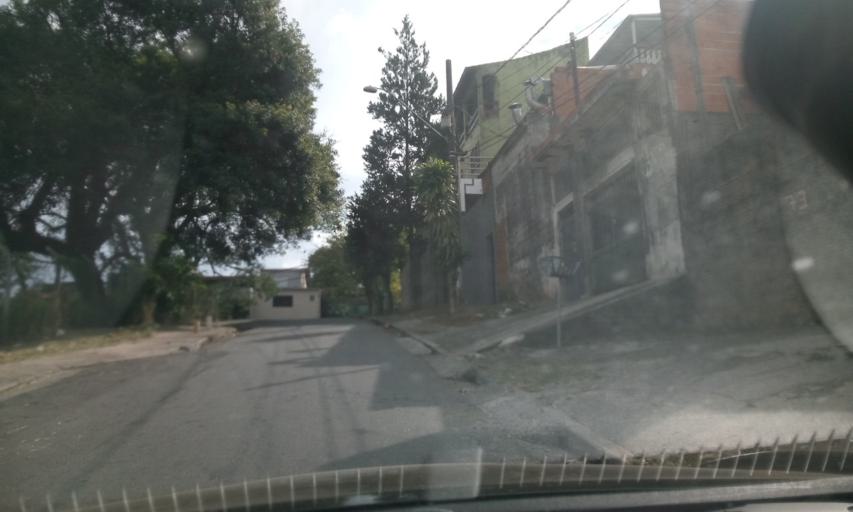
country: BR
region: Sao Paulo
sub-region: Diadema
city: Diadema
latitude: -23.7718
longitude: -46.6098
